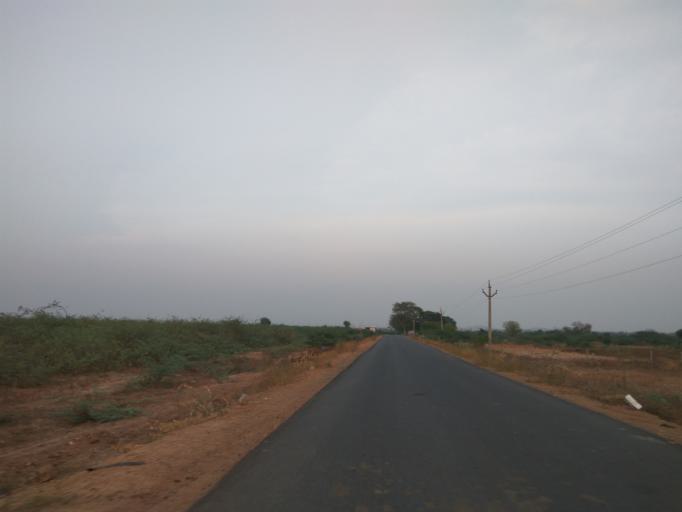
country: IN
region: Andhra Pradesh
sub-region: Prakasam
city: Markapur
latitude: 15.7434
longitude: 79.2387
